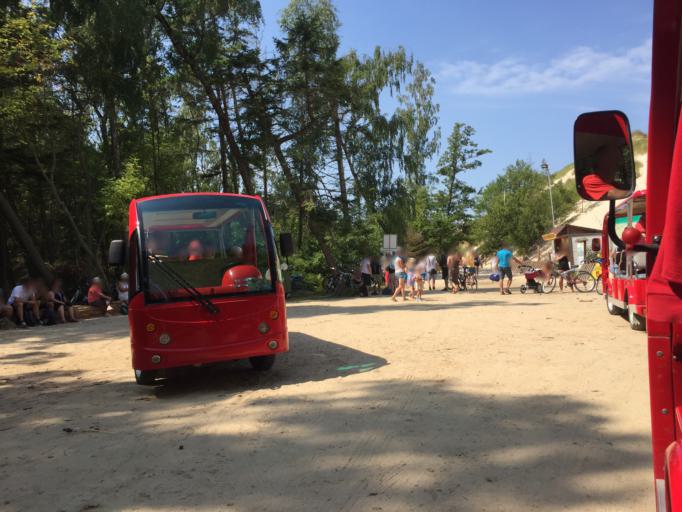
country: PL
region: Pomeranian Voivodeship
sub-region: Powiat leborski
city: Leba
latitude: 54.7486
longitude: 17.4405
